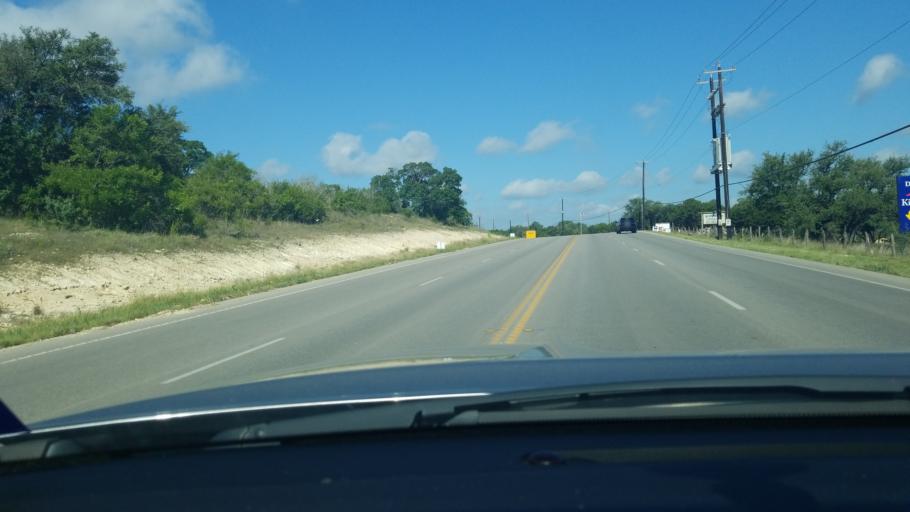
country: US
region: Texas
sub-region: Bexar County
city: Timberwood Park
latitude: 29.7141
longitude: -98.4588
